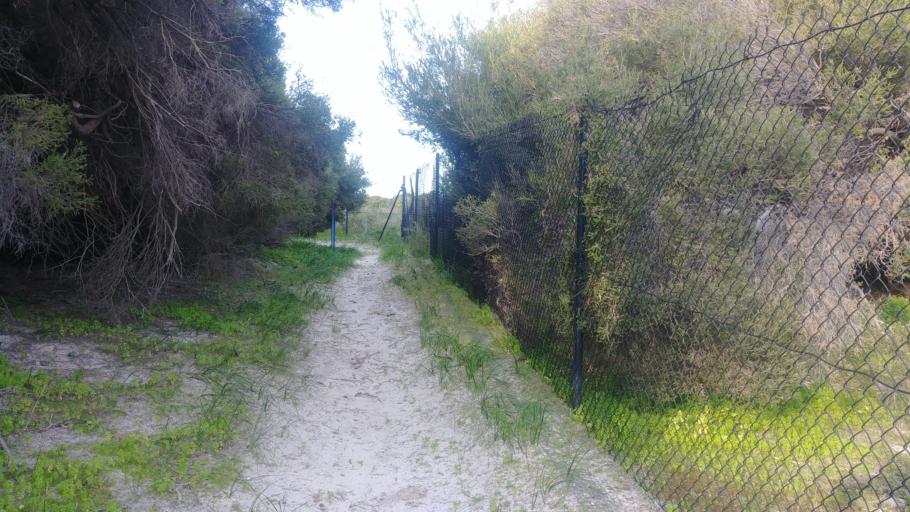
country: AU
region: Western Australia
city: Mosman Park
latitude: -31.9913
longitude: 115.5278
